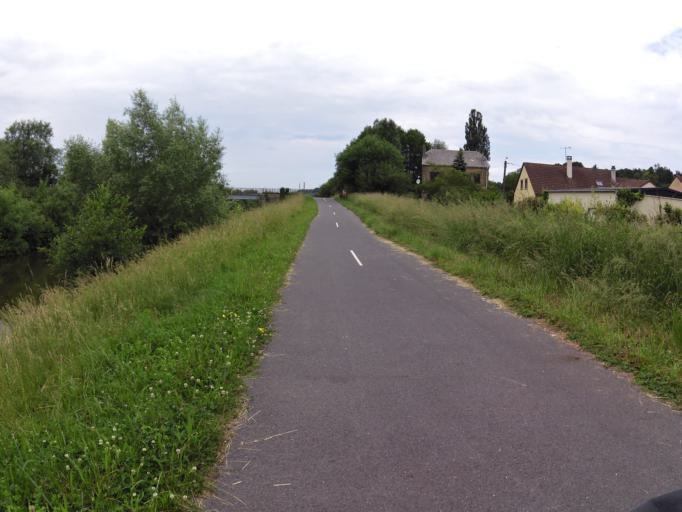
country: FR
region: Champagne-Ardenne
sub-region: Departement des Ardennes
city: Saint-Laurent
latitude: 49.7498
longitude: 4.7682
